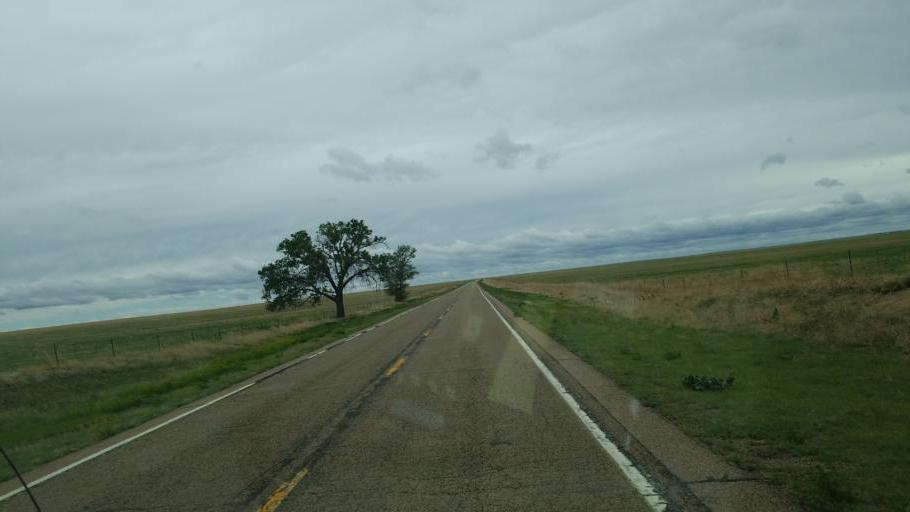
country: US
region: Colorado
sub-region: Lincoln County
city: Hugo
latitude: 38.8521
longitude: -103.7321
